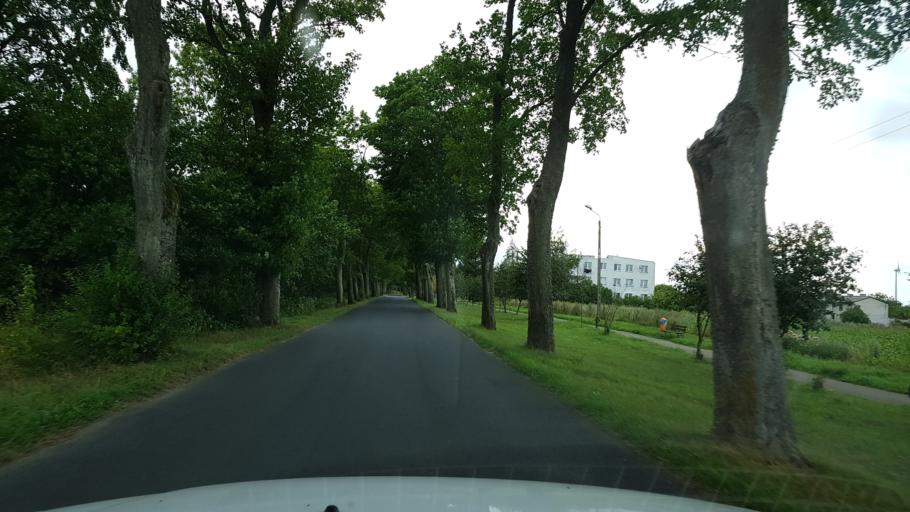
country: PL
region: West Pomeranian Voivodeship
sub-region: Powiat bialogardzki
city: Karlino
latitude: 54.1156
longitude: 15.8284
